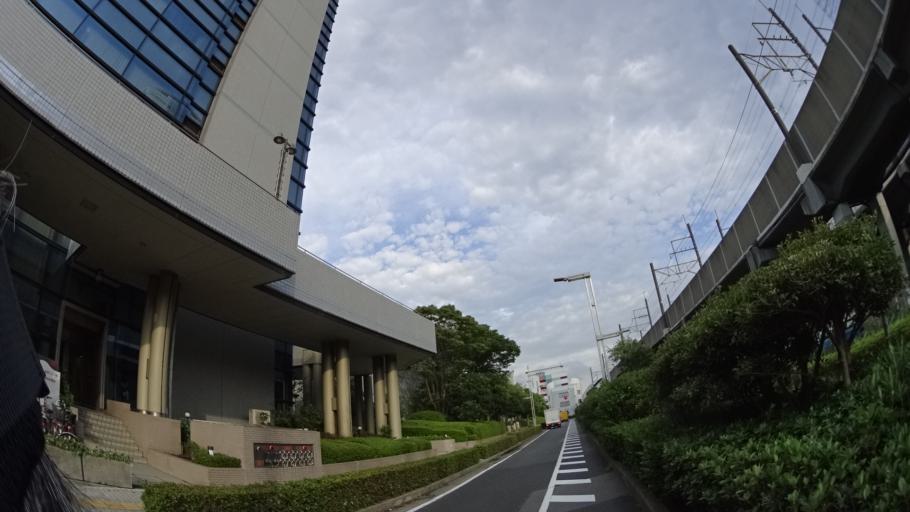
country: JP
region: Chiba
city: Funabashi
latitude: 35.6502
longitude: 140.0400
